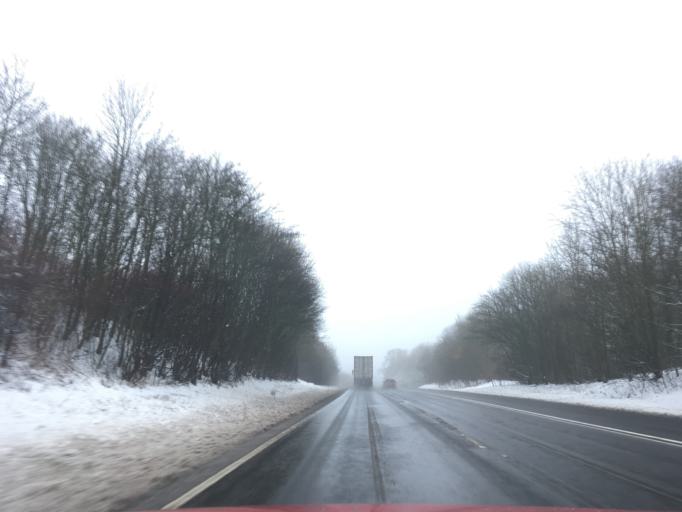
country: GB
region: England
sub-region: Warwickshire
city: Stratford-upon-Avon
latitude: 52.2178
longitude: -1.7109
